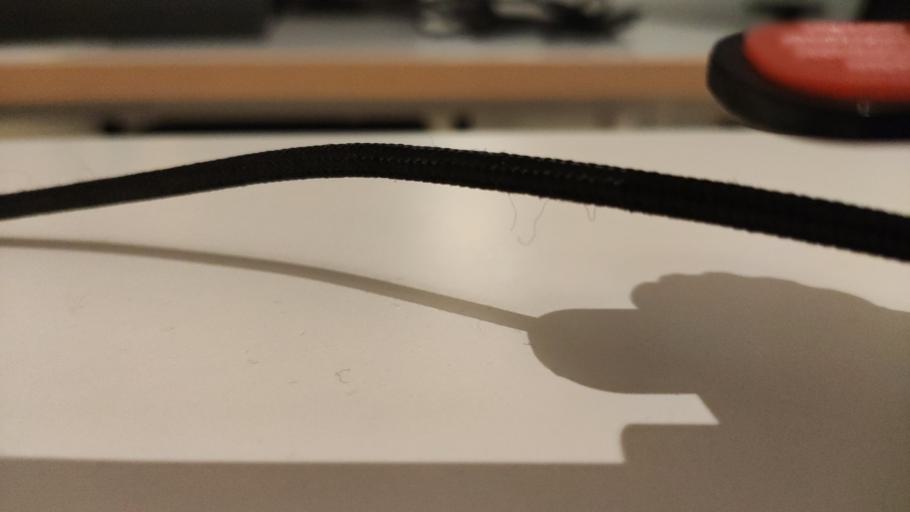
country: RU
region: Moskovskaya
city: Shaburnovo
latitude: 56.4286
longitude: 37.9491
